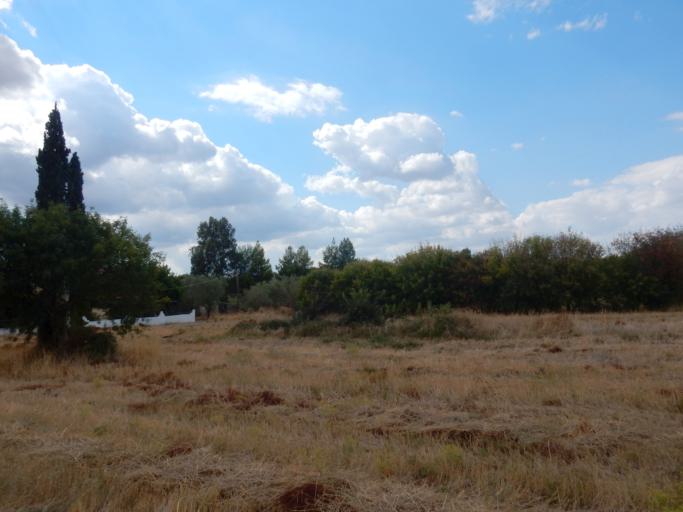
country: GR
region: Attica
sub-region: Nomarchia Anatolikis Attikis
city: Khalkoutsion
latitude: 38.3279
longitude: 23.7521
